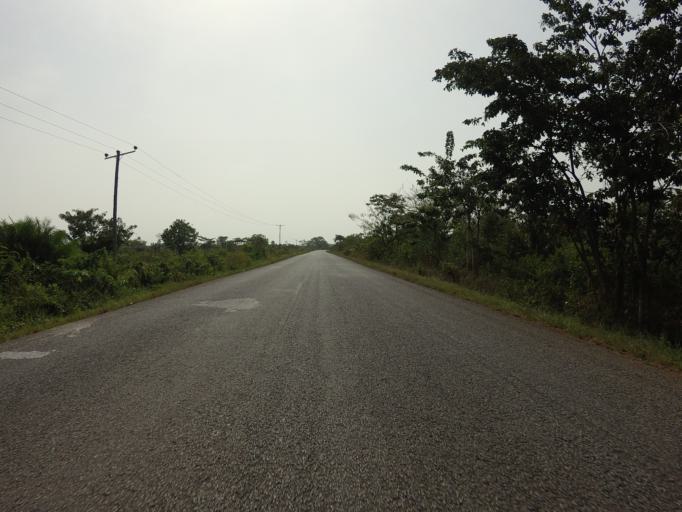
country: GH
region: Volta
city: Ho
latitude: 6.3917
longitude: 0.1823
